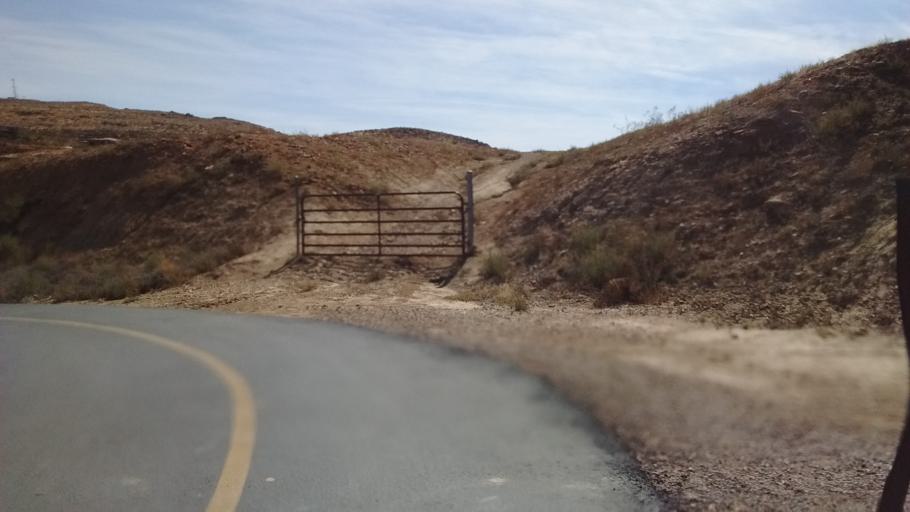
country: US
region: Utah
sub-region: Washington County
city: Saint George
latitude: 37.0736
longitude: -113.5830
